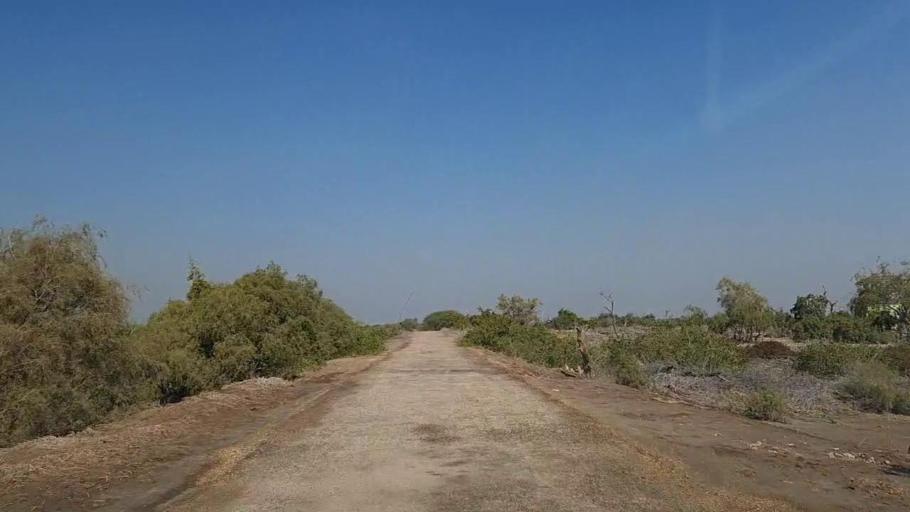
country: PK
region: Sindh
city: Nawabshah
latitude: 26.2971
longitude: 68.3843
